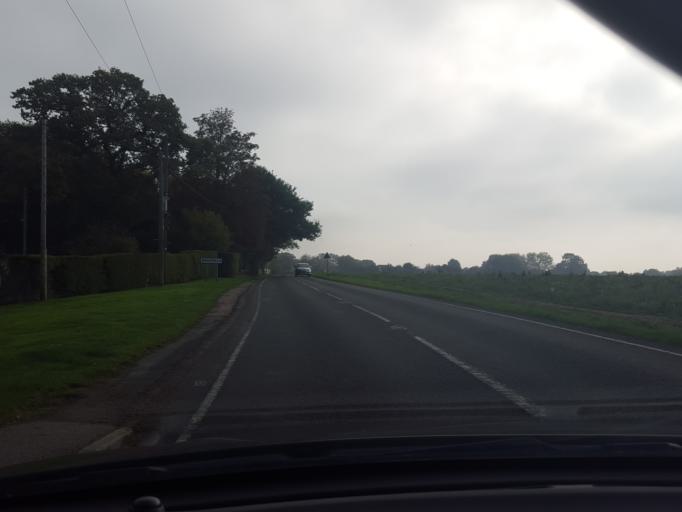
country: GB
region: England
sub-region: Essex
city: Mistley
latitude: 51.9379
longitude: 1.1130
